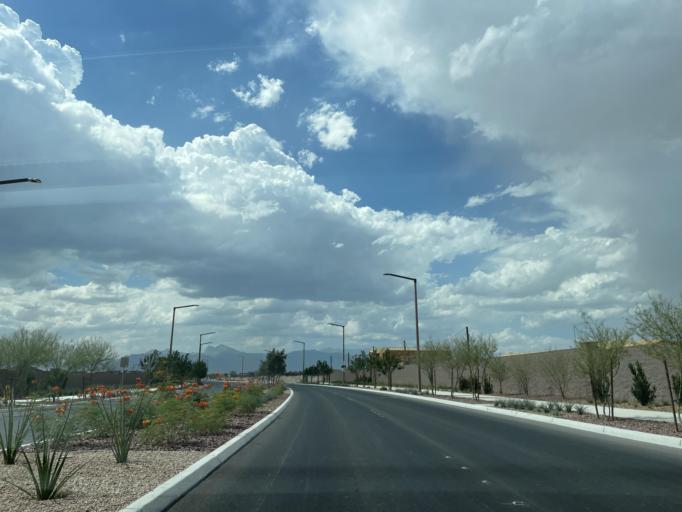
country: US
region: Nevada
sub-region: Clark County
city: North Las Vegas
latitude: 36.3009
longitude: -115.1909
